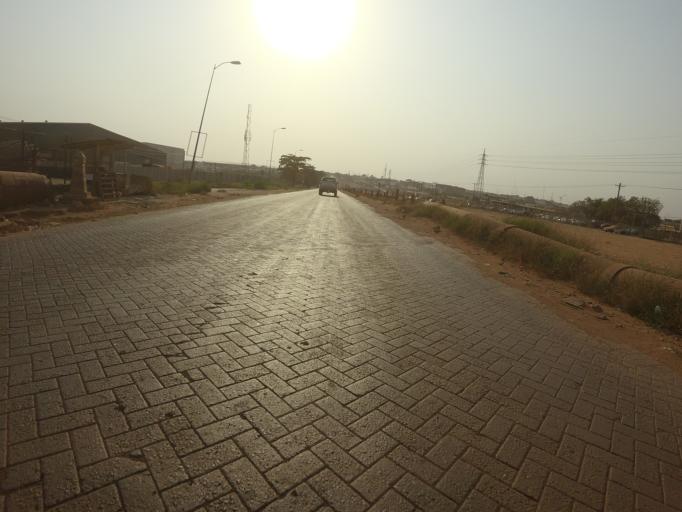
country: GH
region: Greater Accra
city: Tema
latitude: 5.6657
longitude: 0.0072
